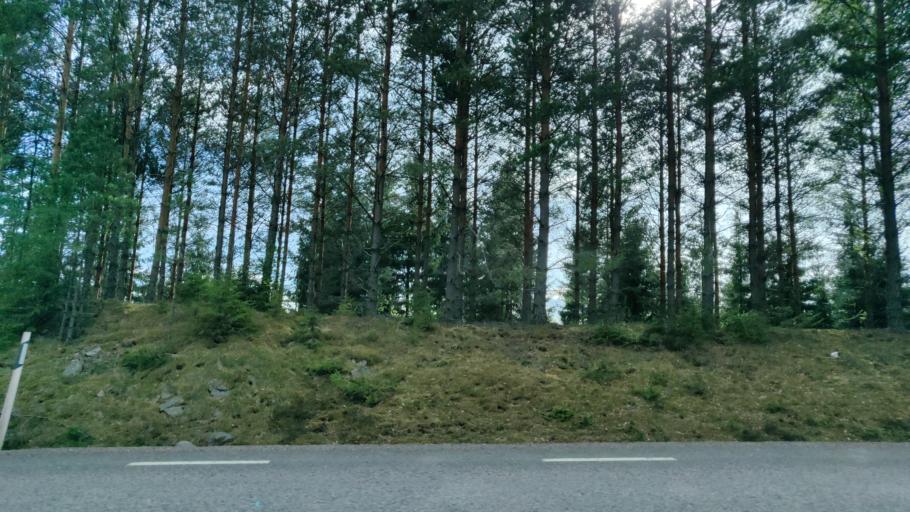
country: SE
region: Vaermland
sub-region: Forshaga Kommun
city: Deje
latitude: 59.5820
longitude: 13.4635
